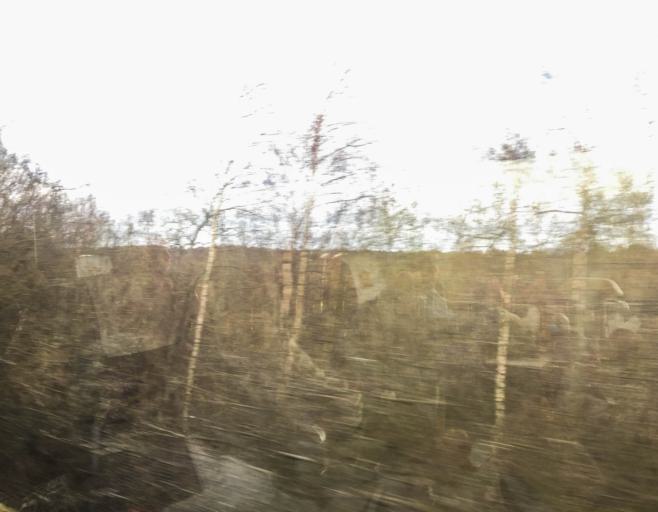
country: GB
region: Scotland
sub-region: North Lanarkshire
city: Newarthill
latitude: 55.7906
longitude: -3.9493
